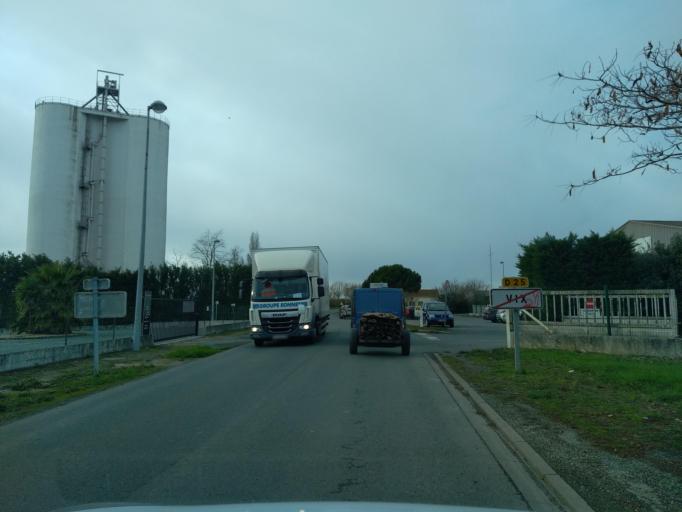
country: FR
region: Pays de la Loire
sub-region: Departement de la Vendee
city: Vix
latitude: 46.3687
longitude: -0.8701
